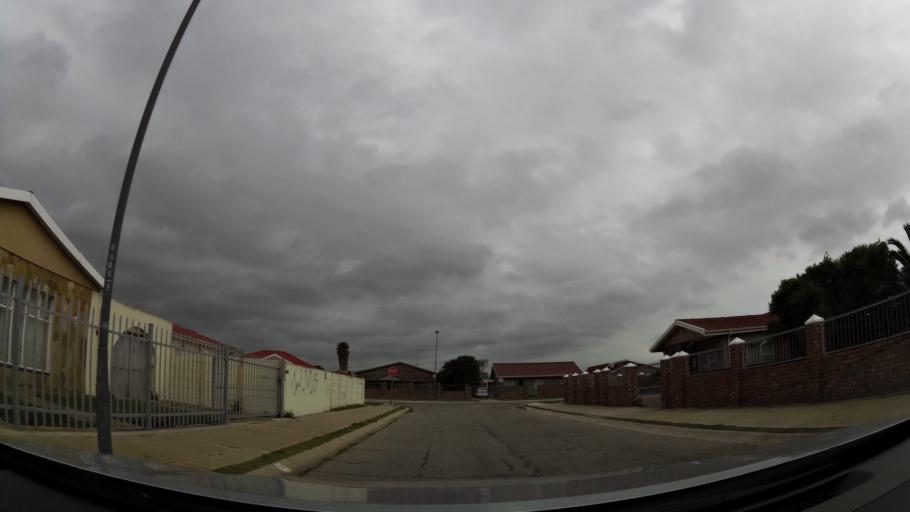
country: ZA
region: Eastern Cape
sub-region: Nelson Mandela Bay Metropolitan Municipality
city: Port Elizabeth
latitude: -33.8972
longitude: 25.5629
